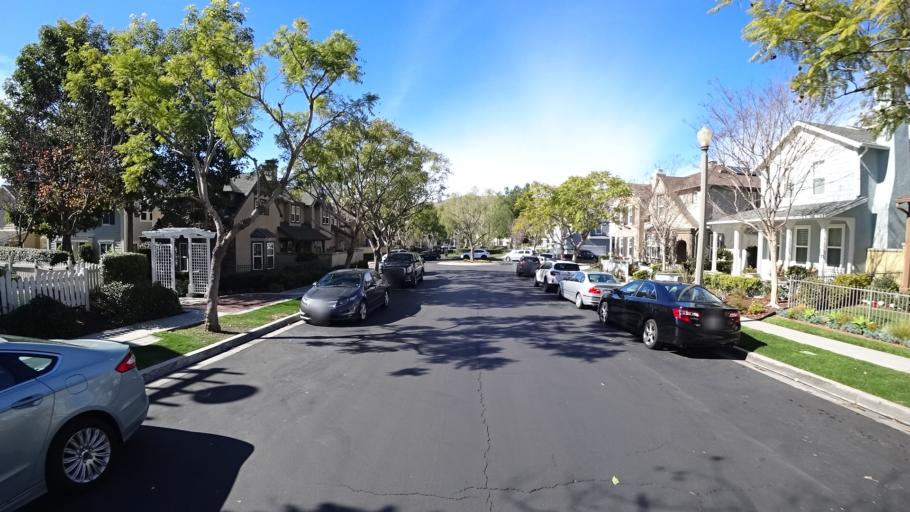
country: US
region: California
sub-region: Orange County
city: Ladera Ranch
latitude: 33.5435
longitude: -117.6448
